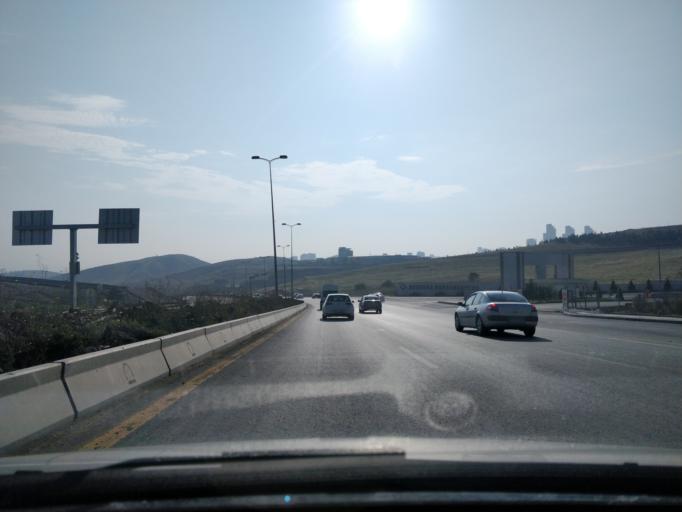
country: TR
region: Ankara
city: Etimesgut
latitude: 39.8969
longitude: 32.6694
